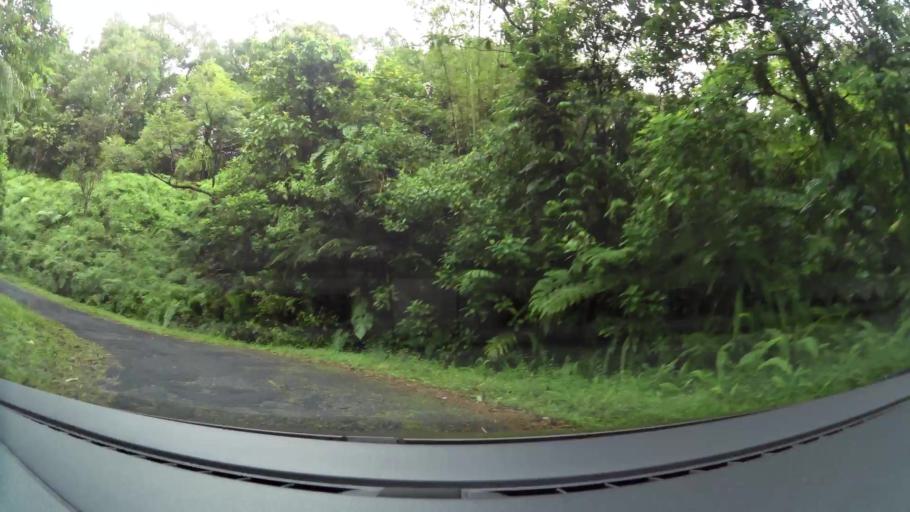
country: GP
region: Guadeloupe
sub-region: Guadeloupe
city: Trois-Rivieres
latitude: 16.0362
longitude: -61.6350
